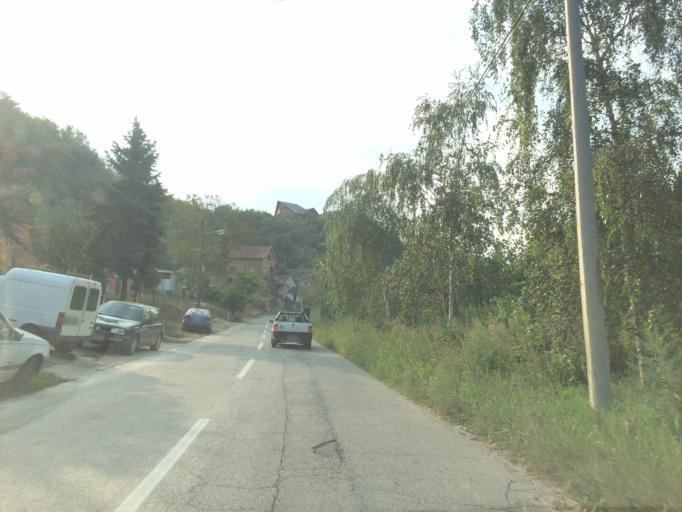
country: RS
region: Autonomna Pokrajina Vojvodina
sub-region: Juznobacki Okrug
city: Novi Sad
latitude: 45.2135
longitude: 19.8072
